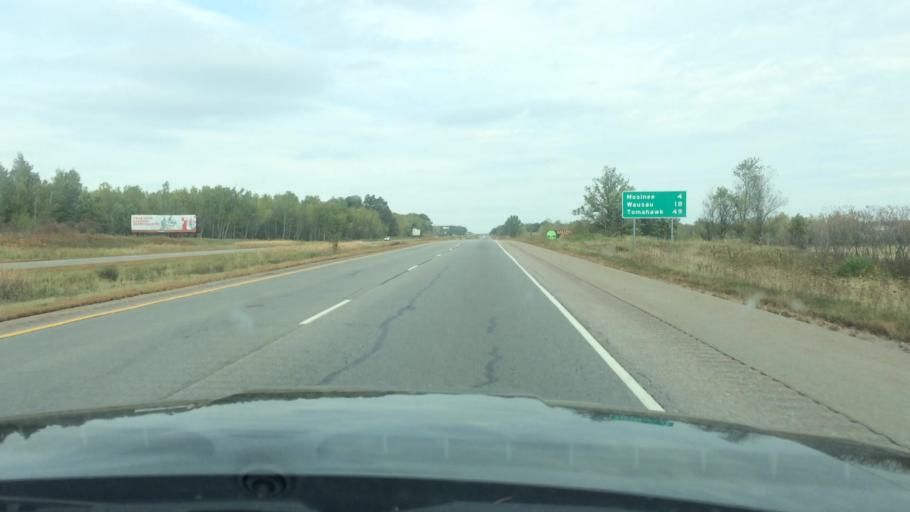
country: US
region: Wisconsin
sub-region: Marathon County
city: Mosinee
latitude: 44.7435
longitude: -89.6796
